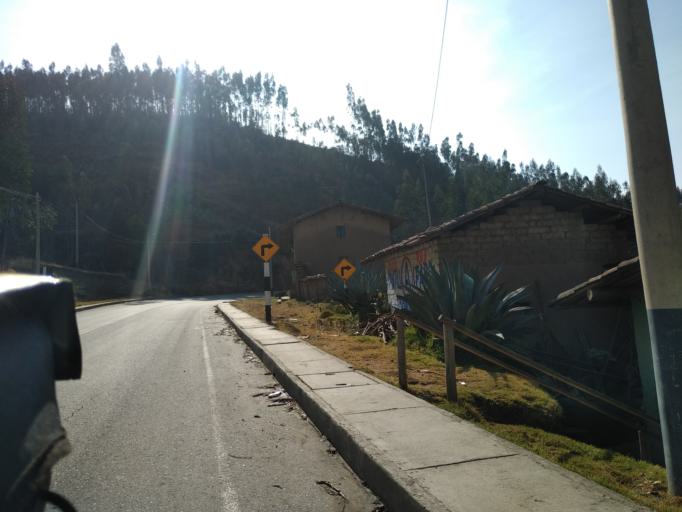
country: PE
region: La Libertad
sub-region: Provincia de Otuzco
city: Mache
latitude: -7.9991
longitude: -78.5072
